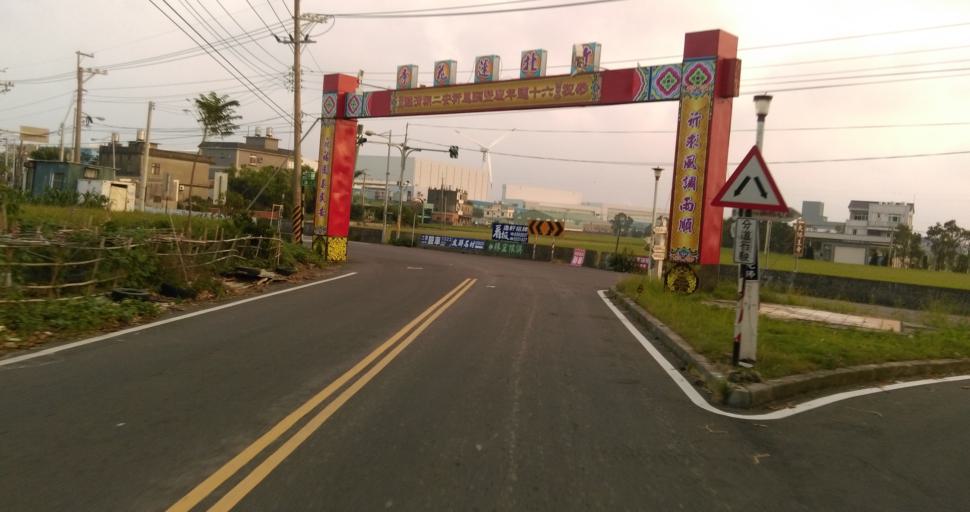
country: TW
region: Taiwan
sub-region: Hsinchu
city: Zhubei
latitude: 24.8620
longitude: 120.9610
